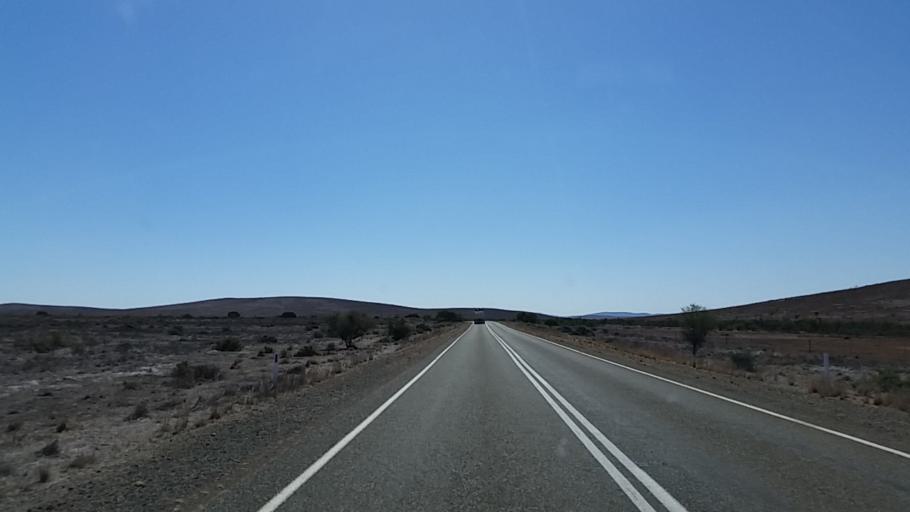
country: AU
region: South Australia
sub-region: Flinders Ranges
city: Quorn
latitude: -32.1443
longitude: 138.5200
